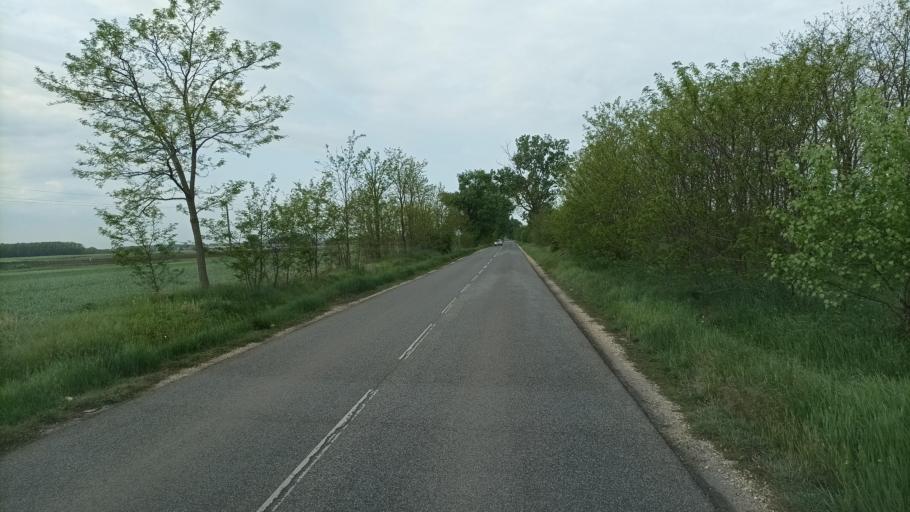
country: HU
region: Pest
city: Monor
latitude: 47.3344
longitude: 19.4188
